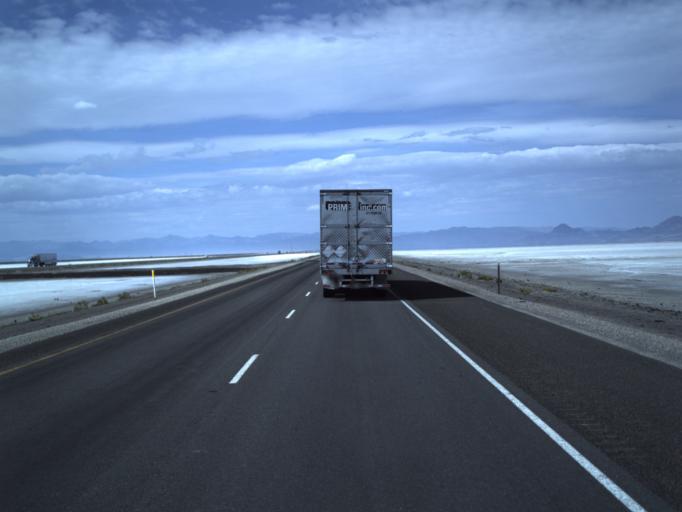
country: US
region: Utah
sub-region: Tooele County
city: Wendover
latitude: 40.7360
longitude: -113.6875
